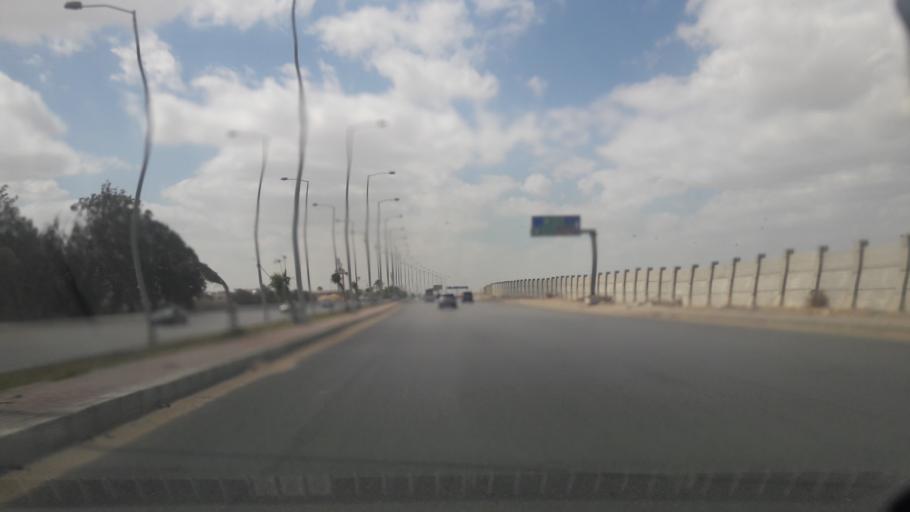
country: EG
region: Al Jizah
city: Al Jizah
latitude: 29.9538
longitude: 31.0830
